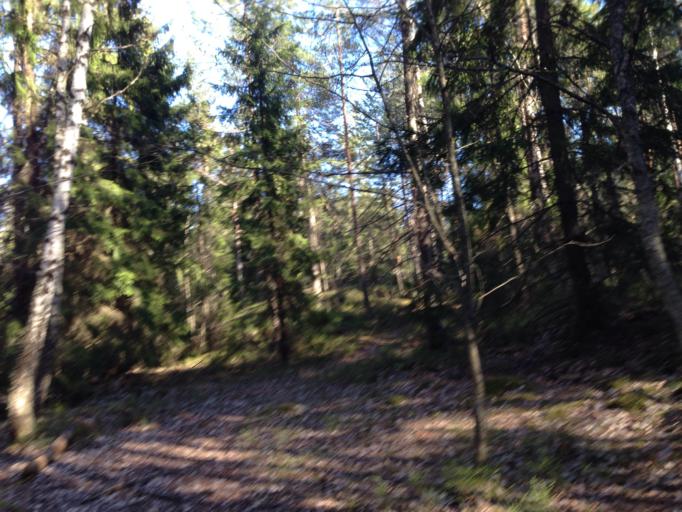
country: SE
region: Stockholm
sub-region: Nacka Kommun
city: Nacka
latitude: 59.2896
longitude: 18.1292
